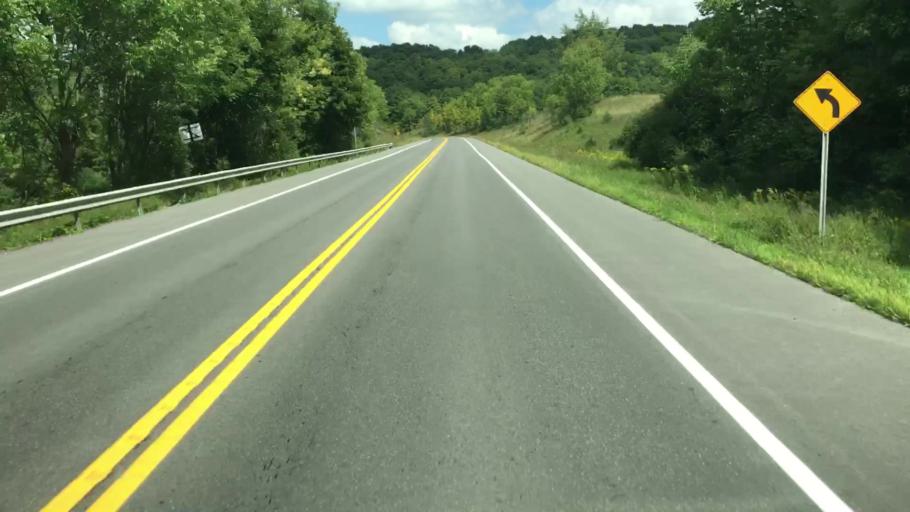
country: US
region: New York
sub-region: Onondaga County
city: Marcellus
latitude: 42.9583
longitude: -76.3387
